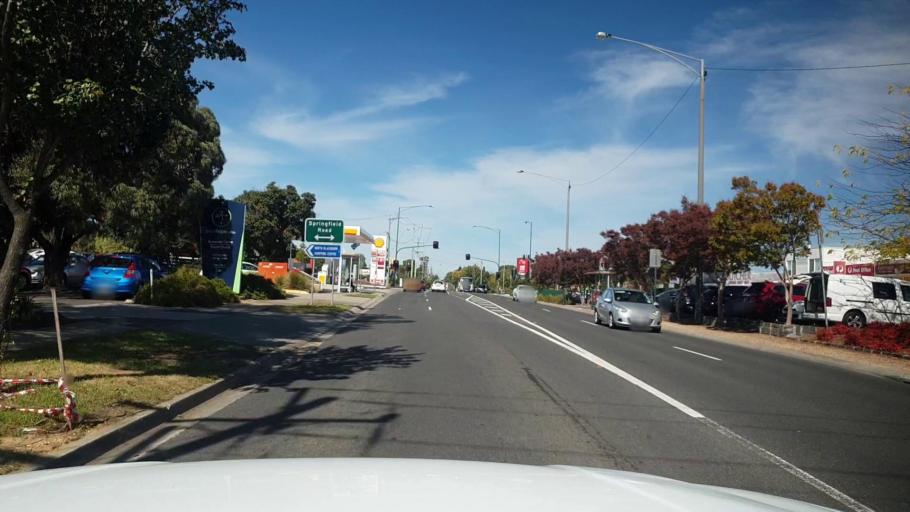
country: AU
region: Victoria
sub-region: Whitehorse
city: Blackburn North
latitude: -37.8081
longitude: 145.1408
